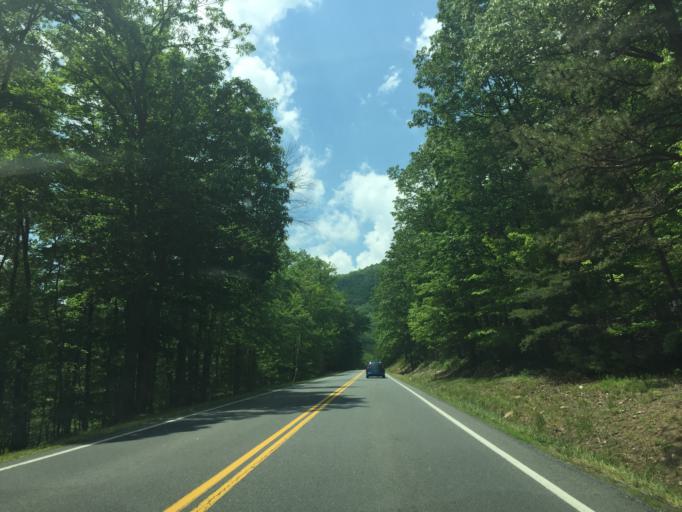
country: US
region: Virginia
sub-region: Frederick County
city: Shawnee Land
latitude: 39.0981
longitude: -78.4637
